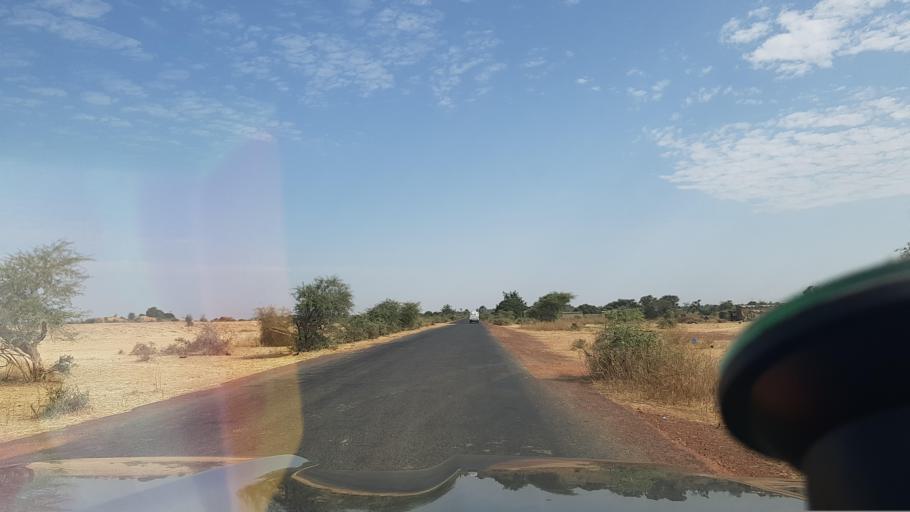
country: ML
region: Segou
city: Markala
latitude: 13.6967
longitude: -6.0972
